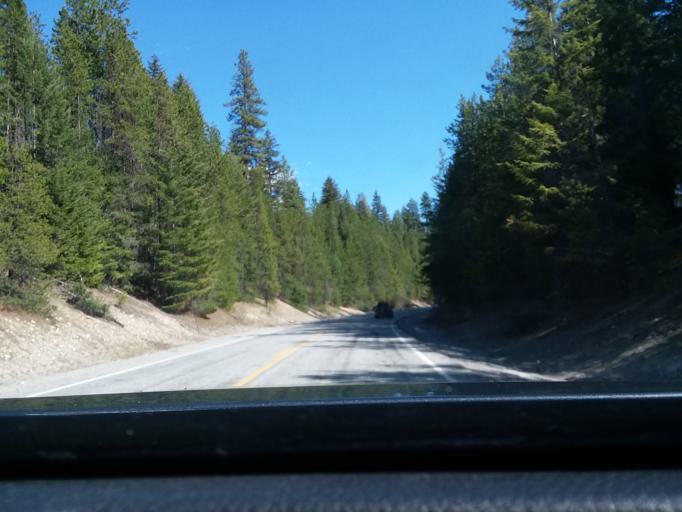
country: US
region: Washington
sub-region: Chelan County
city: Leavenworth
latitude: 47.7955
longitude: -120.6637
